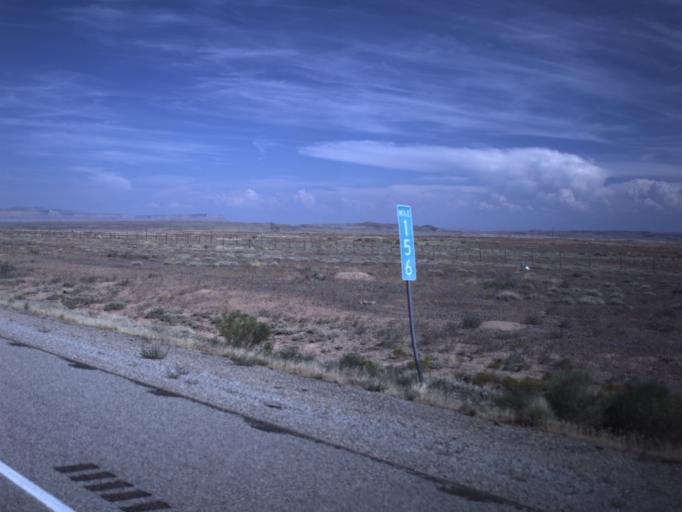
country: US
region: Utah
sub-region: Carbon County
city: East Carbon City
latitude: 38.9694
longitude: -110.2655
